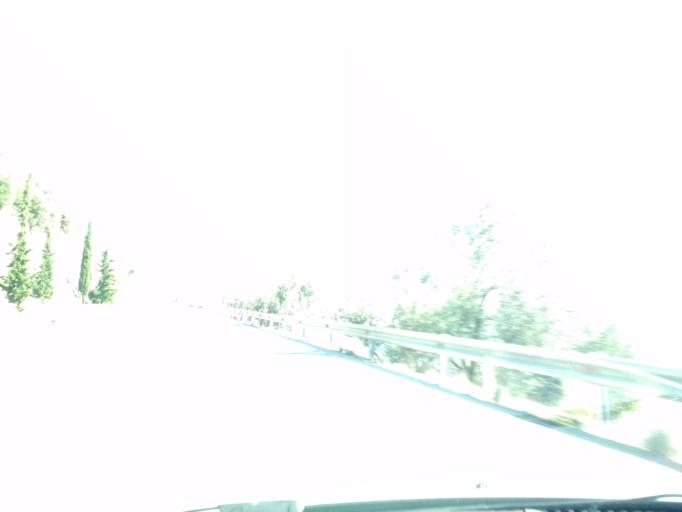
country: GR
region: Central Greece
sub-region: Nomos Evvoias
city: Oreoi
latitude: 38.8444
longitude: 23.0732
